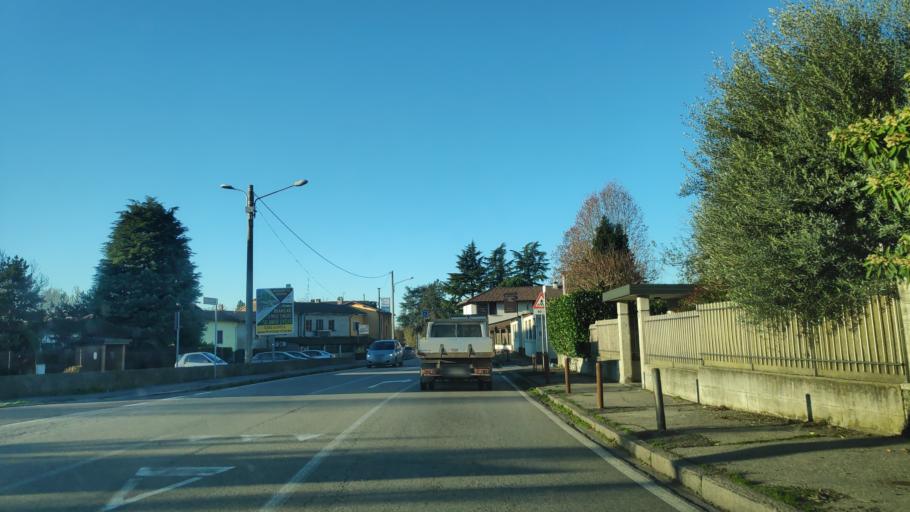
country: IT
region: Lombardy
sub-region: Citta metropolitana di Milano
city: Pieve Emanuele
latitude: 45.3611
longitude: 9.2055
